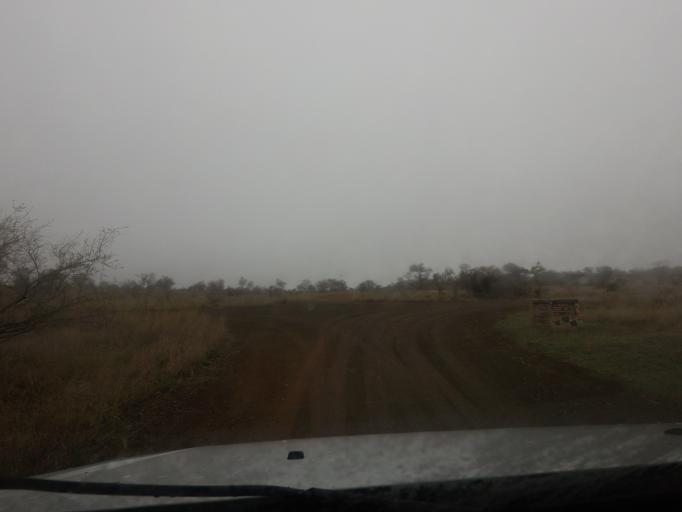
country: ZA
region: Limpopo
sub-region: Mopani District Municipality
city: Phalaborwa
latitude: -24.2633
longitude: 31.6478
